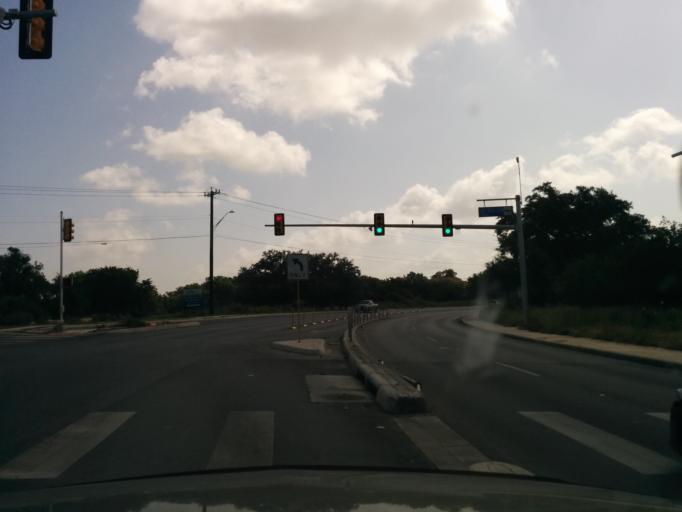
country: US
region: Texas
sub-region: Bexar County
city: Shavano Park
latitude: 29.5624
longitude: -98.6146
